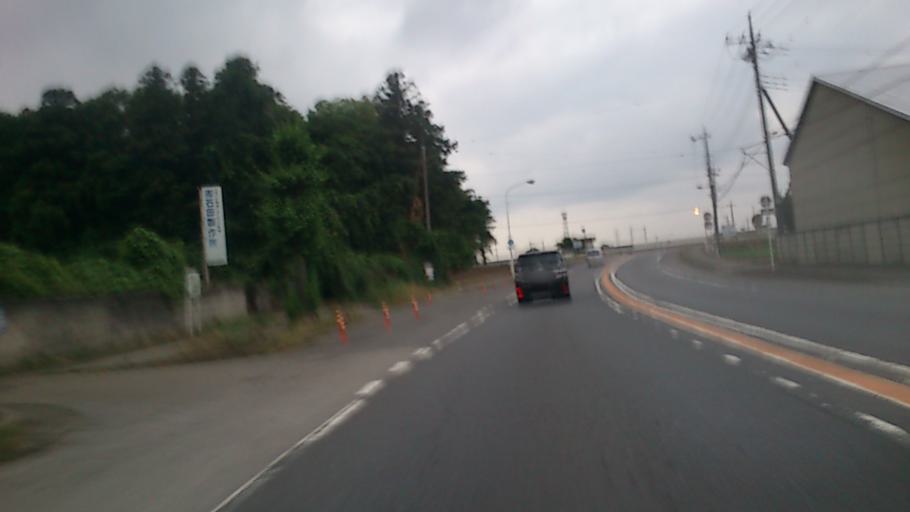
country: JP
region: Ibaraki
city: Koga
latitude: 36.1543
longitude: 139.7340
